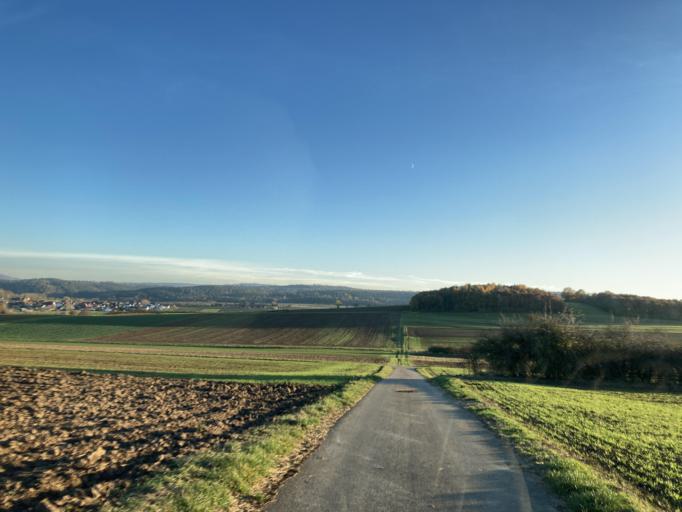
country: DE
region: Baden-Wuerttemberg
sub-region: Tuebingen Region
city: Hirrlingen
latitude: 48.4287
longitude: 8.9042
